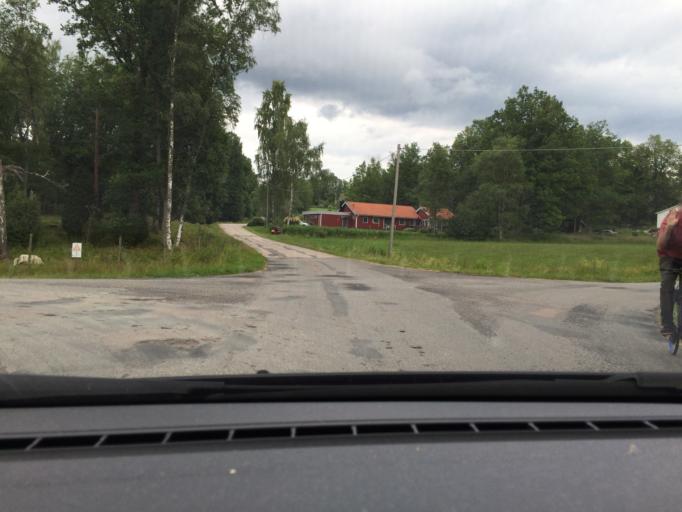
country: SE
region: Joenkoeping
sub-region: Varnamo Kommun
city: Varnamo
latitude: 57.1902
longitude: 13.9438
